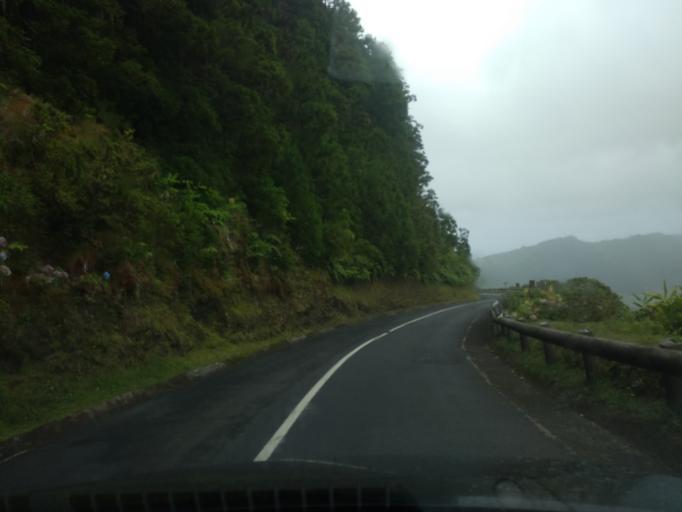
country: PT
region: Azores
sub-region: Ponta Delgada
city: Arrifes
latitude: 37.8381
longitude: -25.7873
